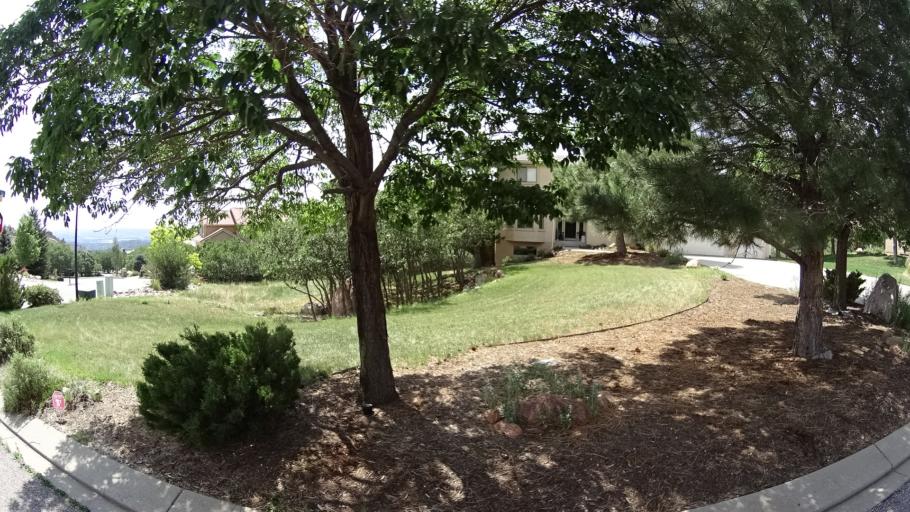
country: US
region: Colorado
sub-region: El Paso County
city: Air Force Academy
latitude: 38.9491
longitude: -104.8844
